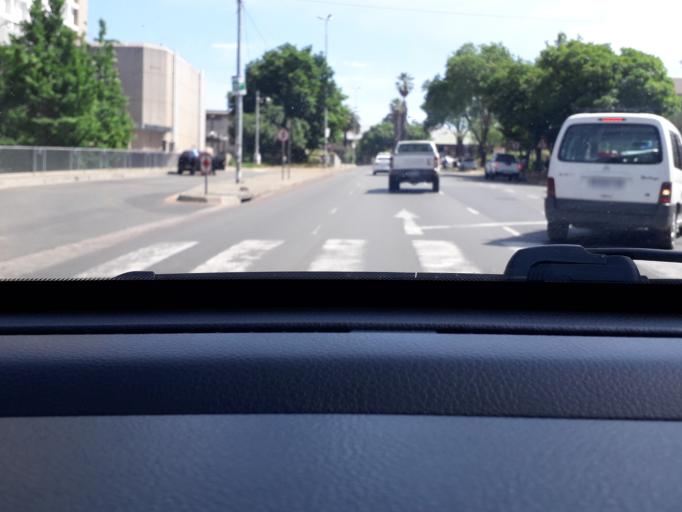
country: ZA
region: Gauteng
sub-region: City of Johannesburg Metropolitan Municipality
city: Johannesburg
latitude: -26.1914
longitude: 28.0391
